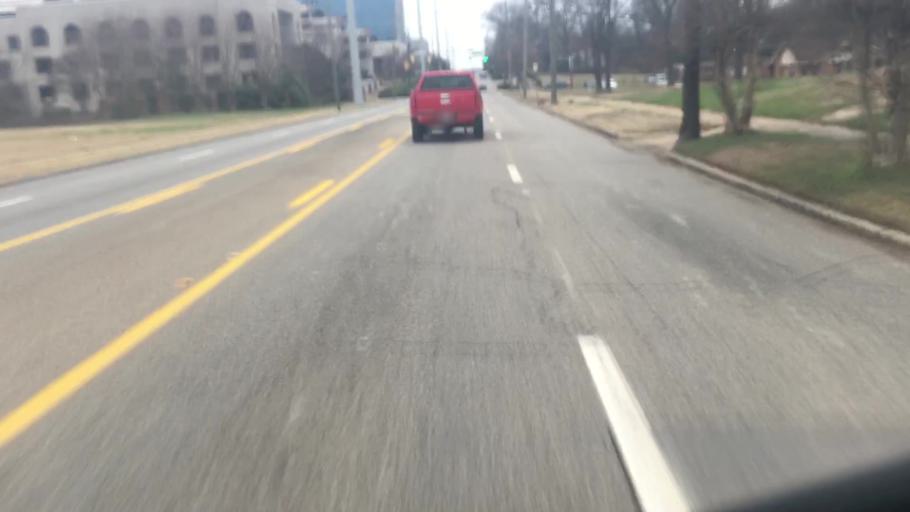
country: US
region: Alabama
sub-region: Jefferson County
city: Birmingham
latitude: 33.5341
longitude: -86.8080
